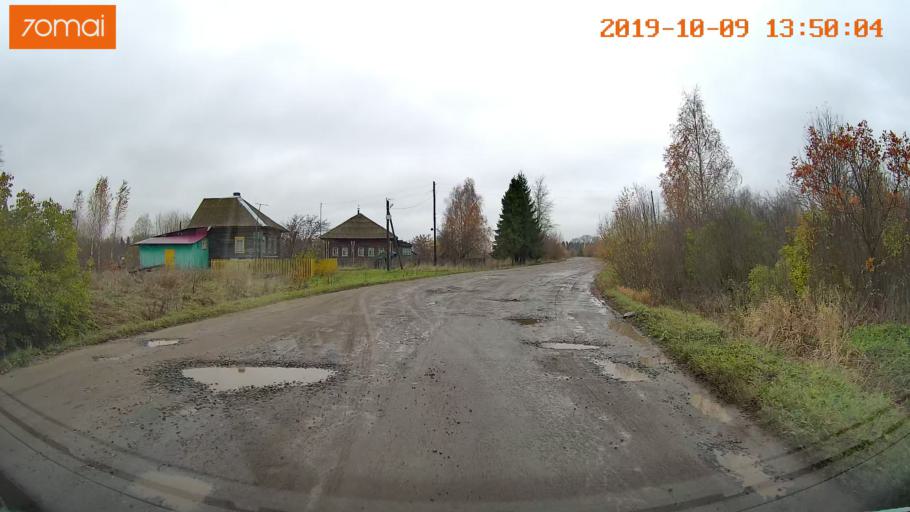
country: RU
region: Kostroma
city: Buy
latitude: 58.4028
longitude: 41.2395
